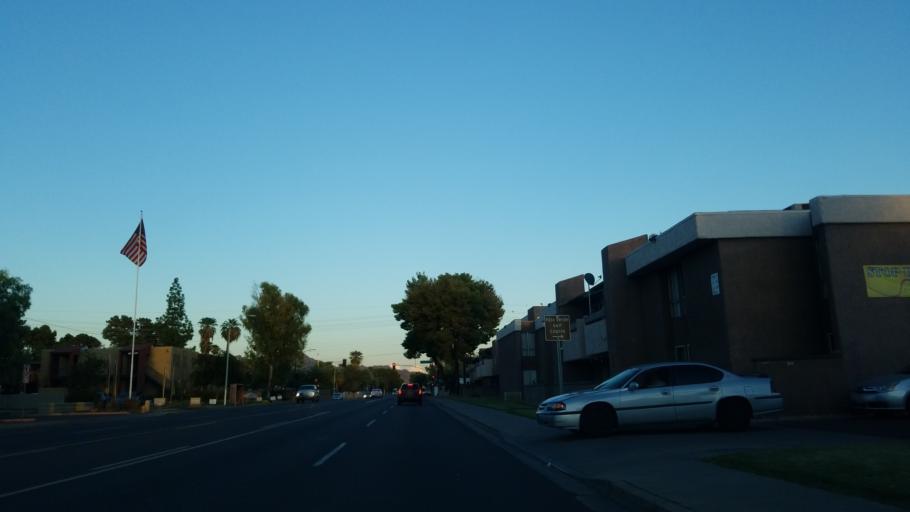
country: US
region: Arizona
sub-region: Maricopa County
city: Glendale
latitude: 33.5385
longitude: -112.0967
